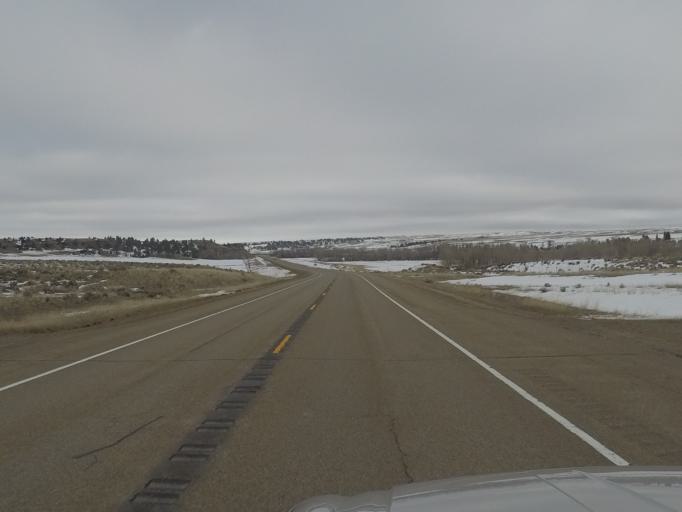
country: US
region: Montana
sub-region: Golden Valley County
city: Ryegate
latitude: 46.3112
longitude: -109.1274
